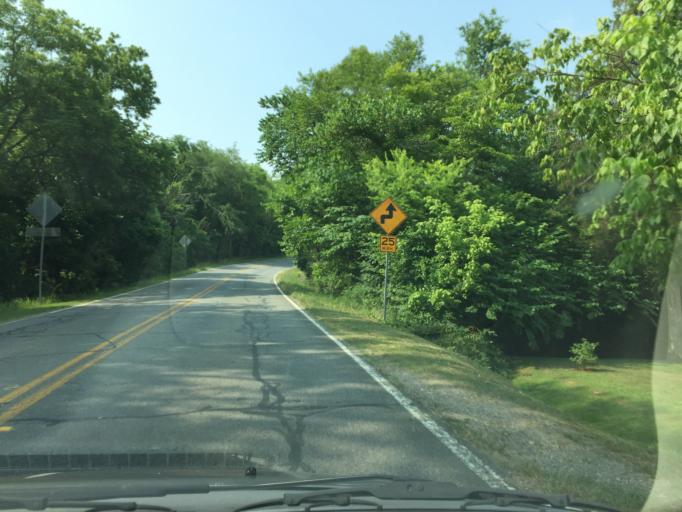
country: US
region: Georgia
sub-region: Catoosa County
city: Ringgold
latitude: 34.9200
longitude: -85.1044
